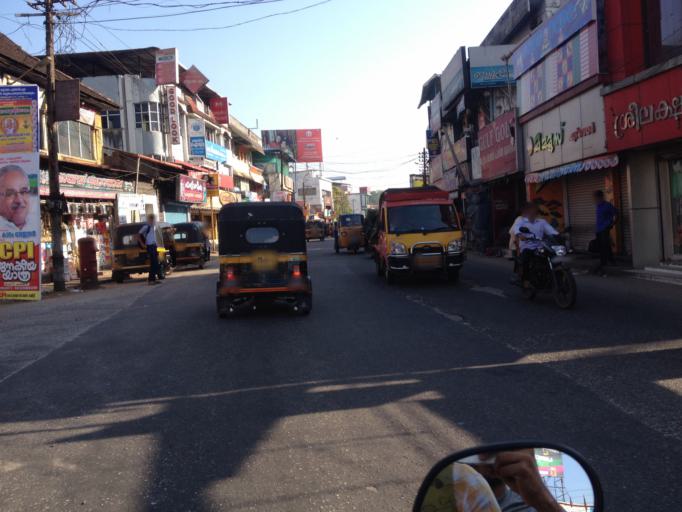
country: IN
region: Kerala
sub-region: Kollam
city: Punalur
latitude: 9.0036
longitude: 76.7739
